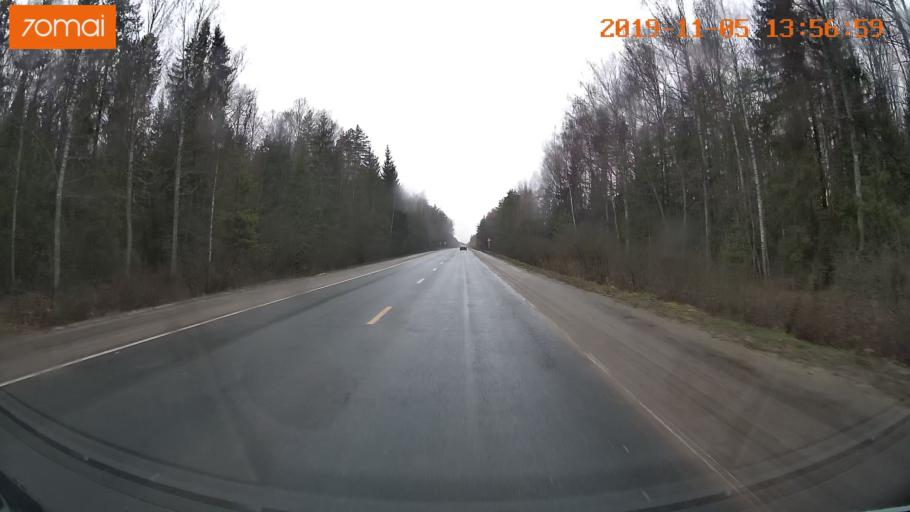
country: RU
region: Ivanovo
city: Kitovo
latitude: 57.0349
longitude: 41.3199
